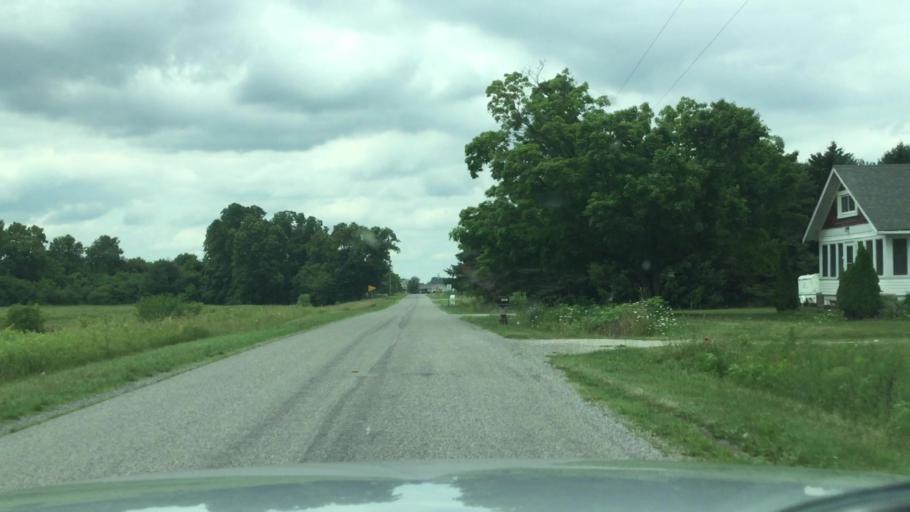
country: US
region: Michigan
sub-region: Saginaw County
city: Burt
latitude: 43.2596
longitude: -83.8767
